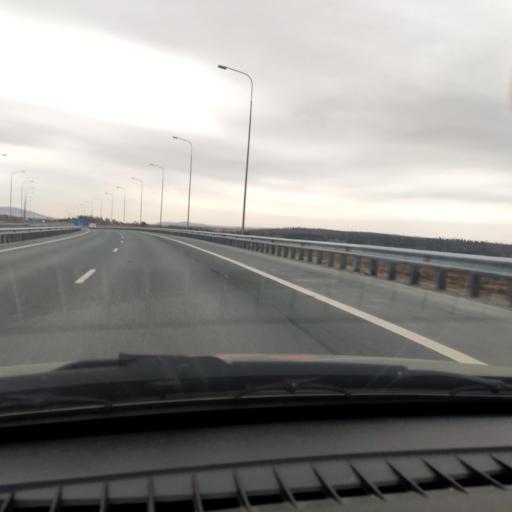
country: RU
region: Samara
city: Bereza
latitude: 53.4988
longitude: 50.1167
